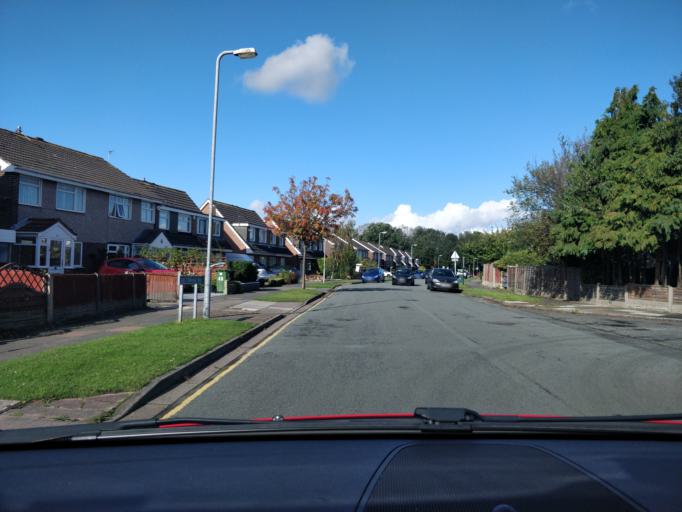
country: GB
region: England
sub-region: Sefton
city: Southport
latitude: 53.6313
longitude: -2.9750
